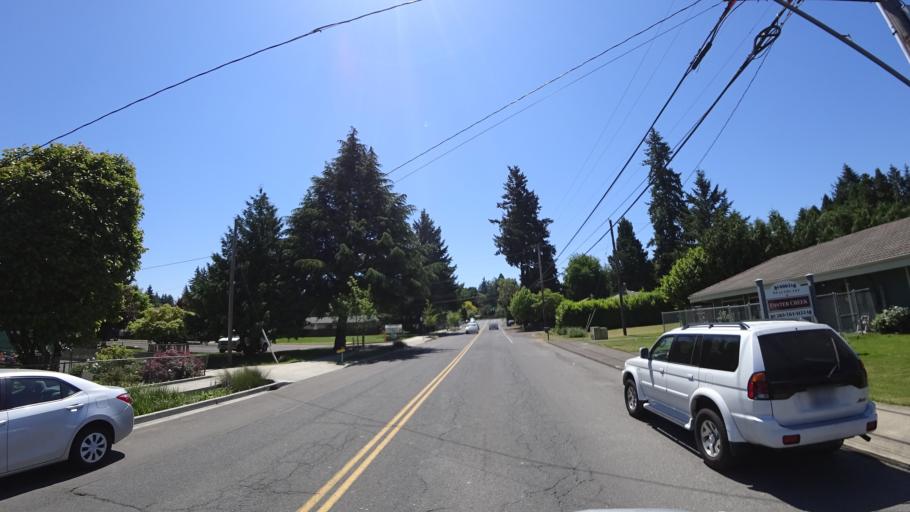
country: US
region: Oregon
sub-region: Clackamas County
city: Happy Valley
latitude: 45.4787
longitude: -122.5236
